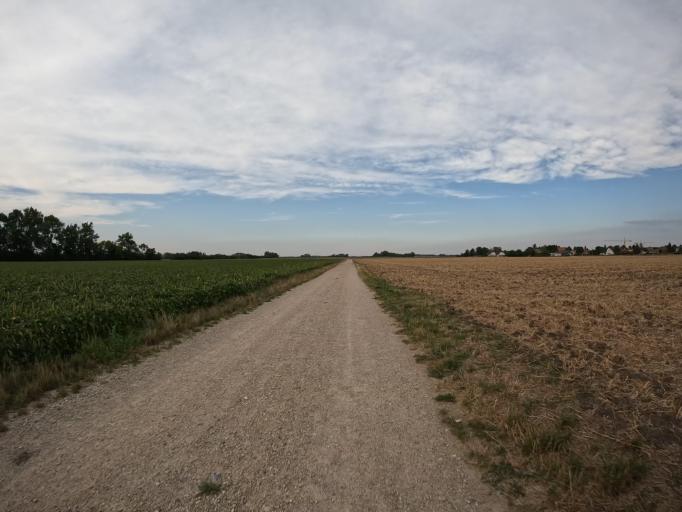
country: AT
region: Lower Austria
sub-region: Politischer Bezirk Baden
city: Trumau
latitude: 48.0006
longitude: 16.3372
